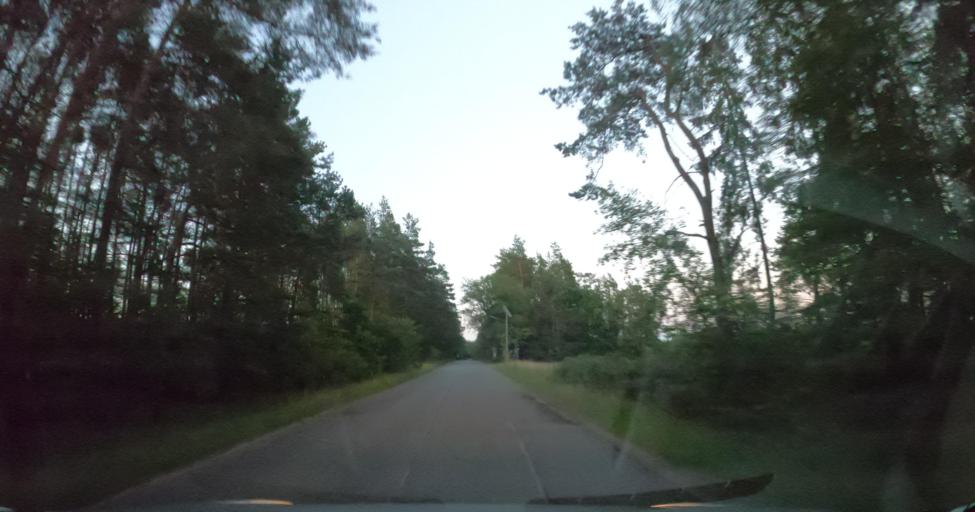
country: PL
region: Pomeranian Voivodeship
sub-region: Powiat wejherowski
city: Szemud
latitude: 54.4708
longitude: 18.1625
